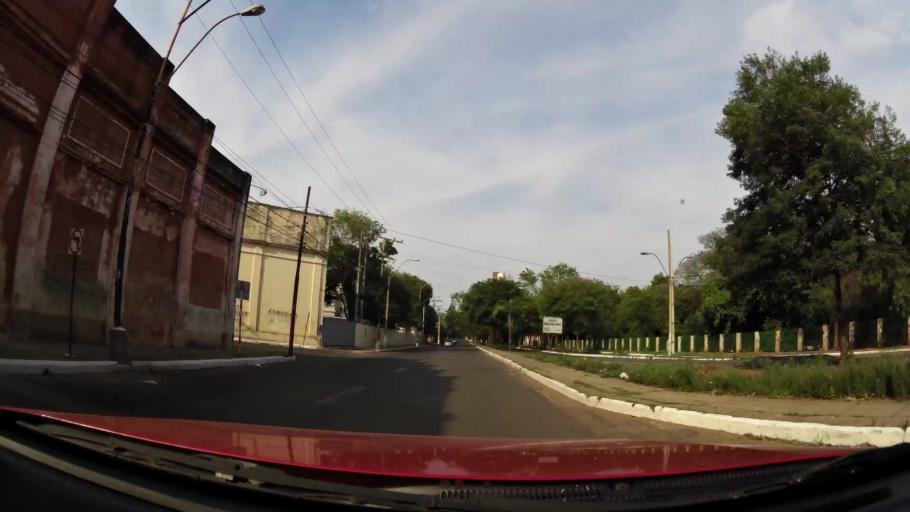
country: PY
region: Asuncion
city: Asuncion
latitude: -25.2814
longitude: -57.6179
